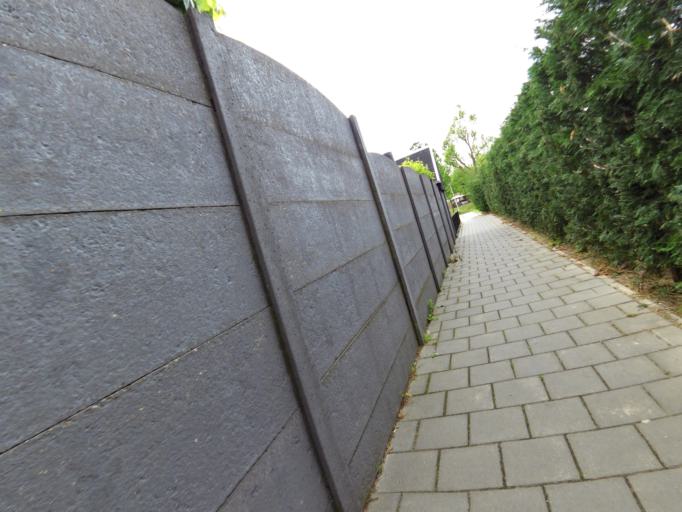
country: NL
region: Limburg
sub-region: Gemeente Kerkrade
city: Kerkrade
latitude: 50.8689
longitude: 6.0217
